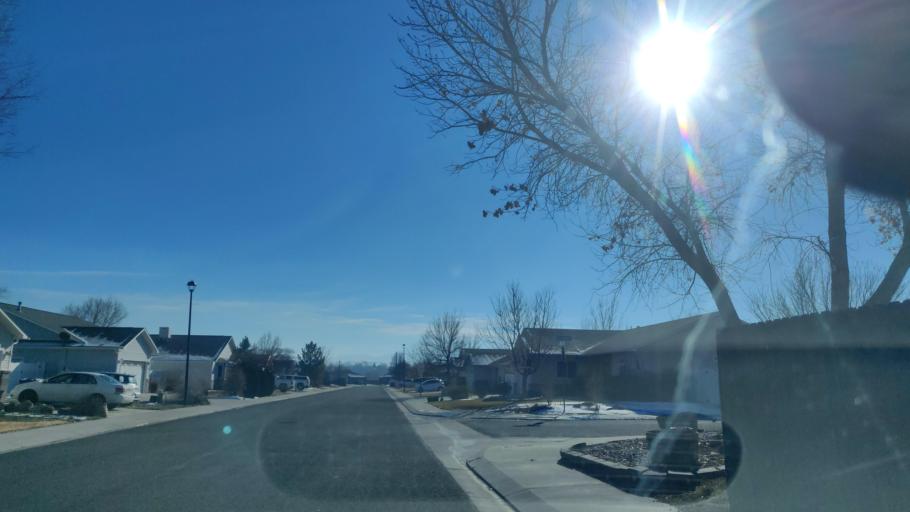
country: US
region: Colorado
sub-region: Mesa County
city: Grand Junction
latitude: 39.0619
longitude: -108.5214
